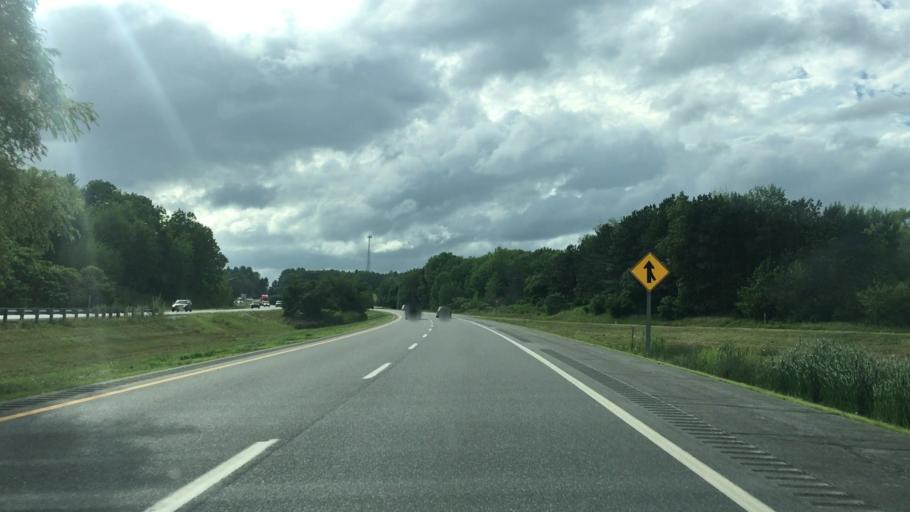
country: US
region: Maine
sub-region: Penobscot County
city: Newport
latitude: 44.8344
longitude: -69.2925
